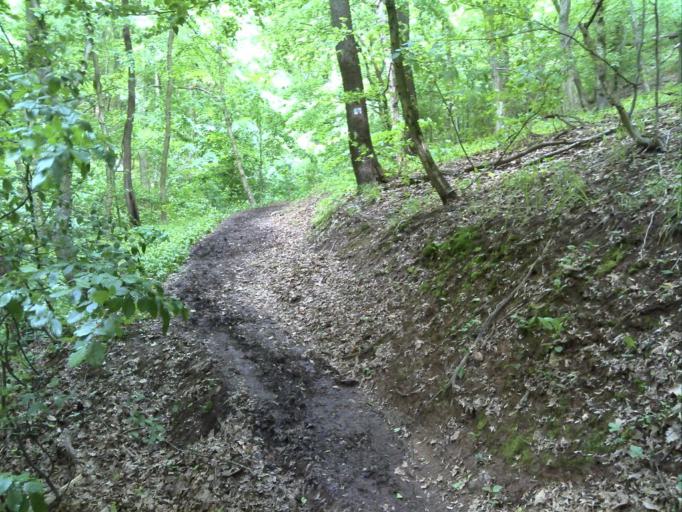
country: HU
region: Baranya
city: Pecs
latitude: 46.0942
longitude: 18.1737
